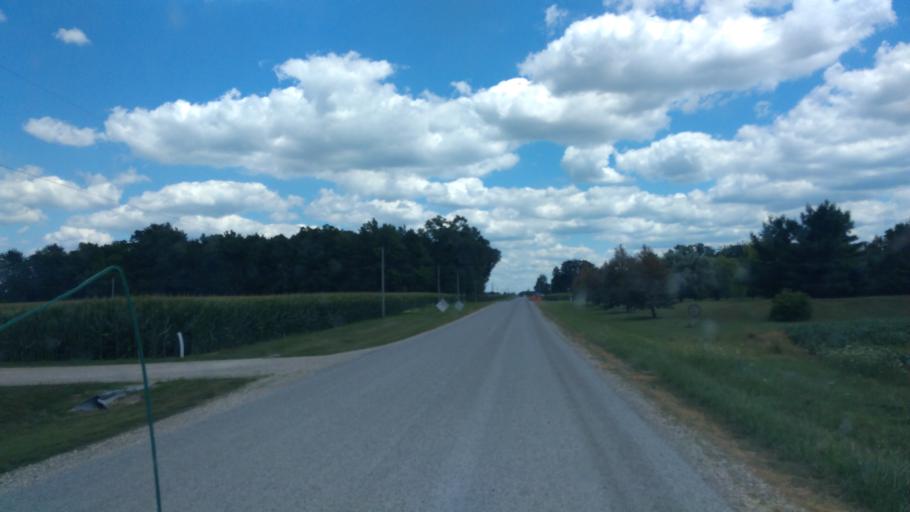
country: US
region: Indiana
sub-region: Adams County
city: Geneva
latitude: 40.5910
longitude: -85.0142
